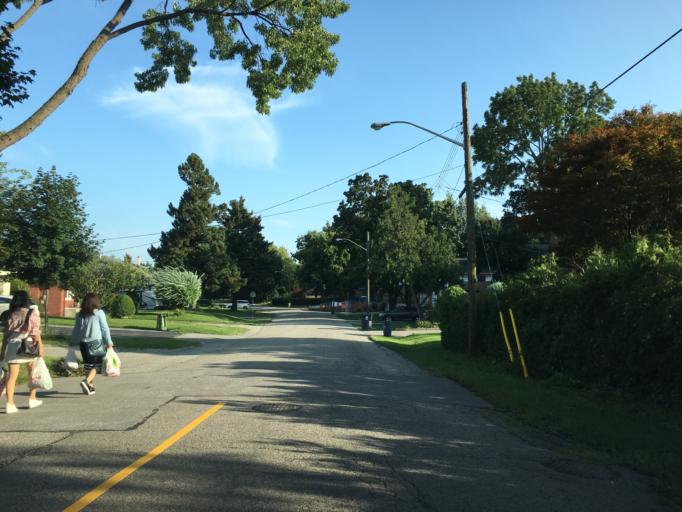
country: CA
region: Ontario
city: Scarborough
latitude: 43.7884
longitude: -79.2825
